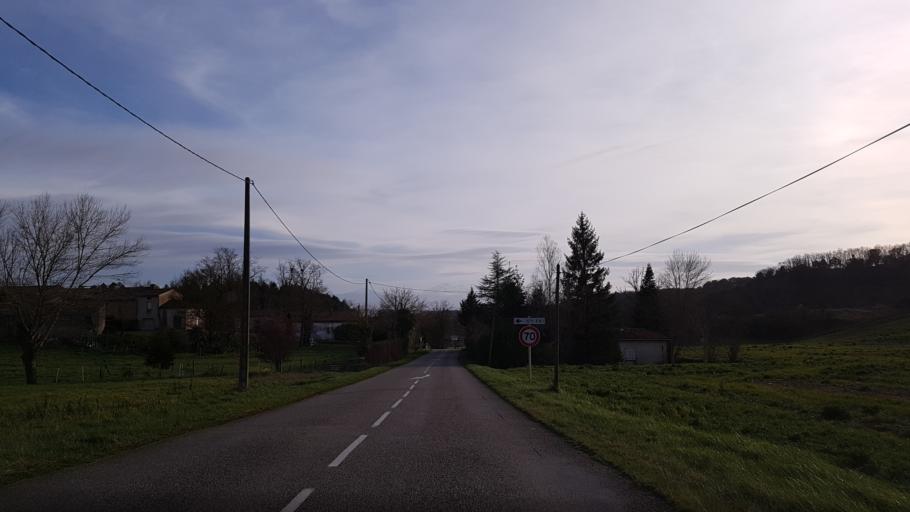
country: FR
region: Midi-Pyrenees
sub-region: Departement de l'Ariege
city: Mirepoix
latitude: 43.1305
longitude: 1.9145
